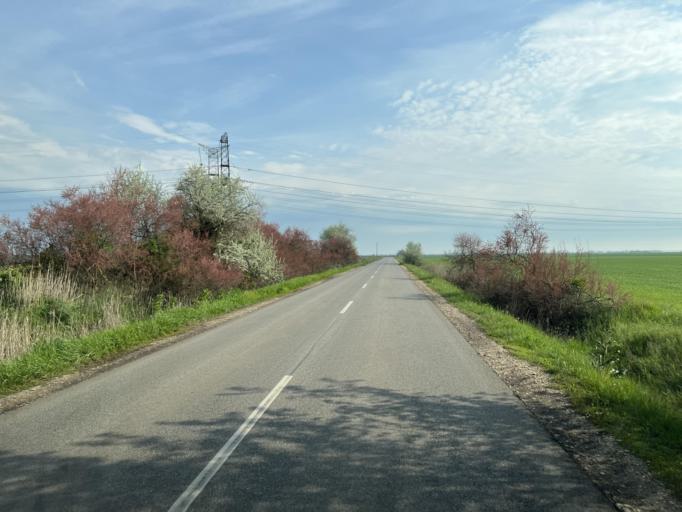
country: HU
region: Pest
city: Cegled
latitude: 47.2343
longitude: 19.7757
